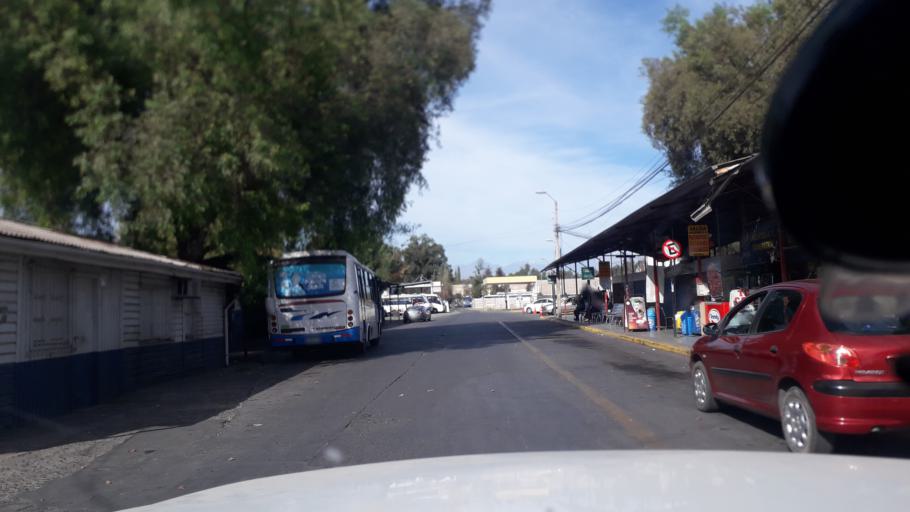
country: CL
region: Valparaiso
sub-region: Provincia de San Felipe
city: San Felipe
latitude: -32.7534
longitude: -70.7205
